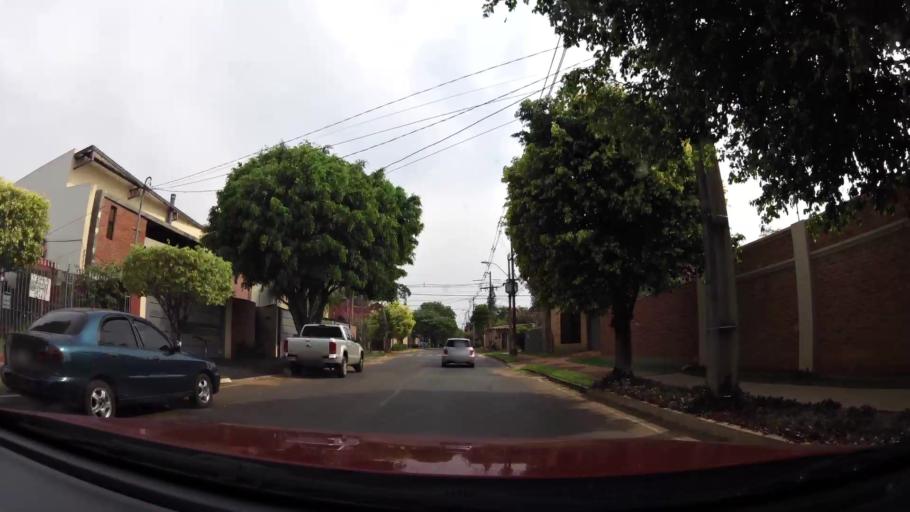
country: PY
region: Central
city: Fernando de la Mora
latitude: -25.2965
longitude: -57.5576
